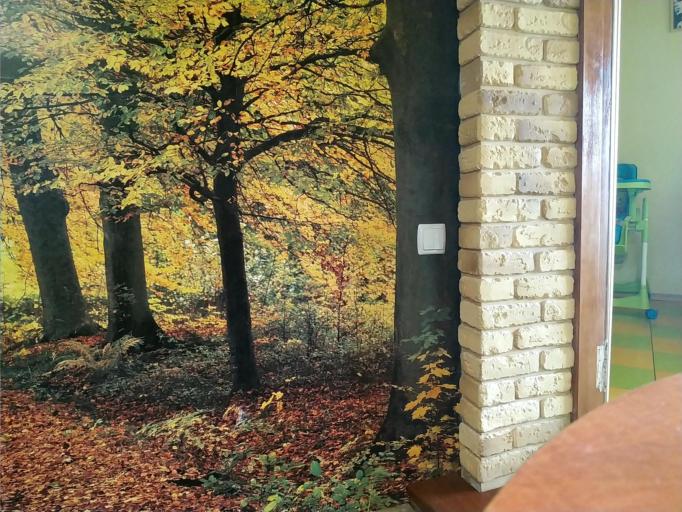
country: RU
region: Smolensk
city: Ozernyy
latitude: 55.4686
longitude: 32.6657
